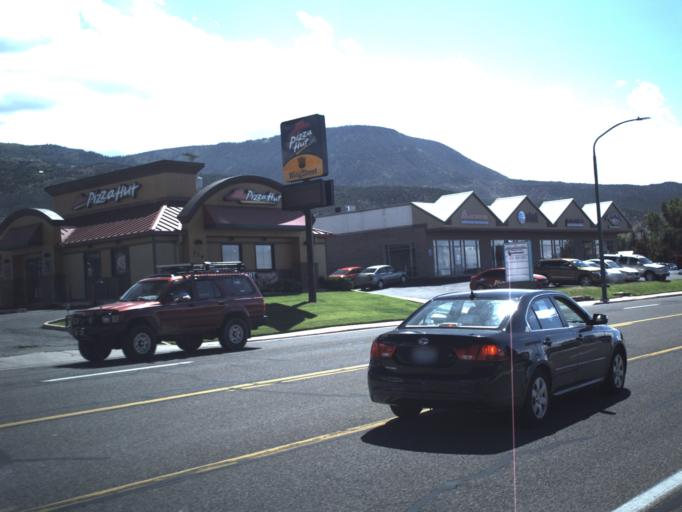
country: US
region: Utah
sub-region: Iron County
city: Cedar City
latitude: 37.6676
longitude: -113.0626
